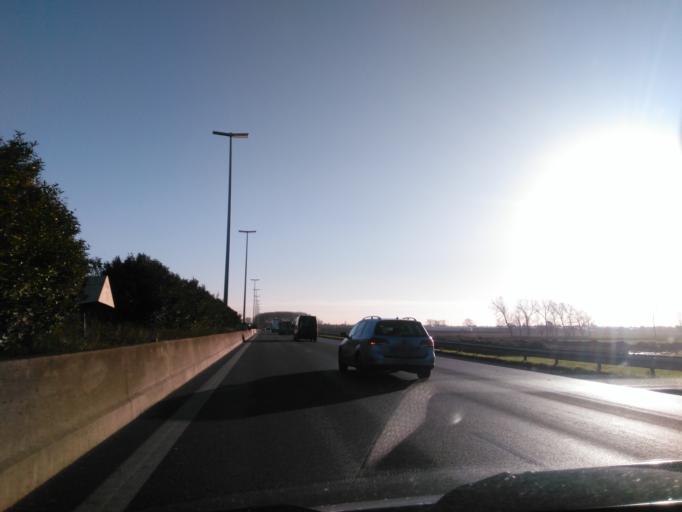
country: BE
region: Flanders
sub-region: Provincie Antwerpen
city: Zwijndrecht
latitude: 51.2331
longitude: 4.3102
